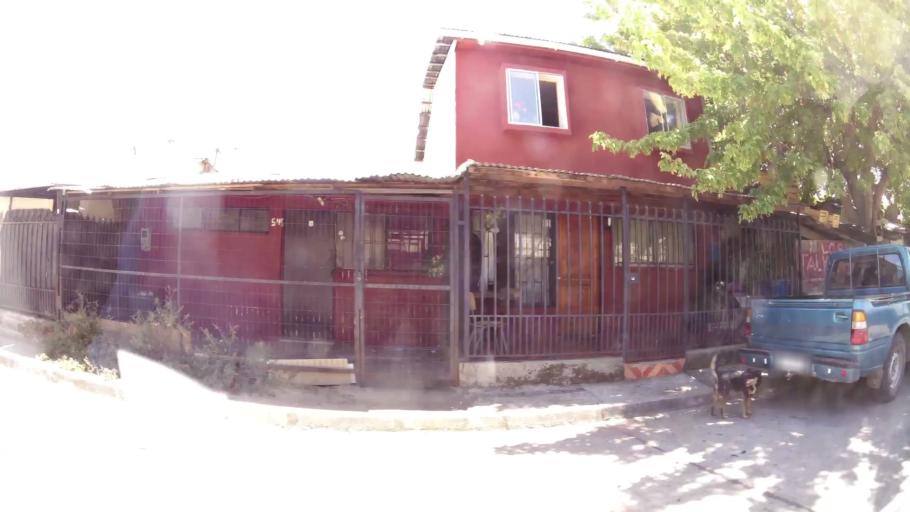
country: CL
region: Maule
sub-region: Provincia de Talca
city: Talca
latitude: -35.4385
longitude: -71.6327
